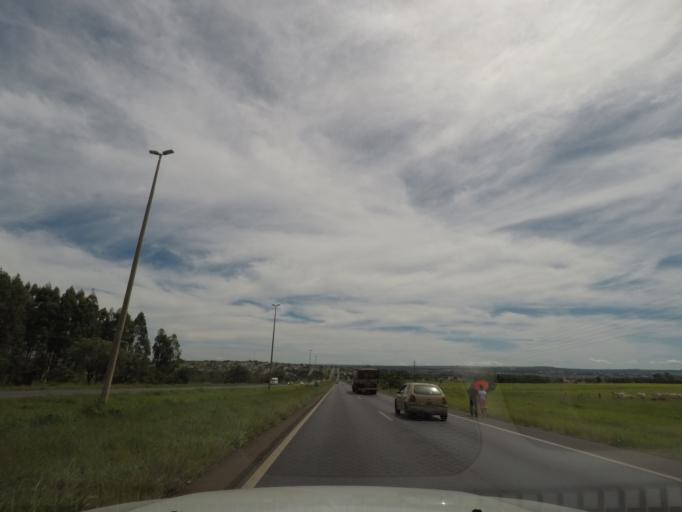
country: BR
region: Goias
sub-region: Planaltina
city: Planaltina
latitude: -15.6127
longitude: -47.7015
